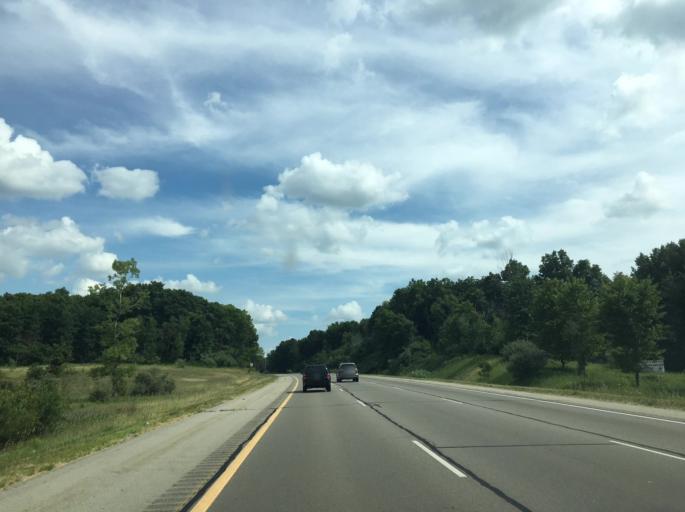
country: US
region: Michigan
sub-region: Oakland County
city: Clarkston
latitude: 42.7529
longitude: -83.5023
